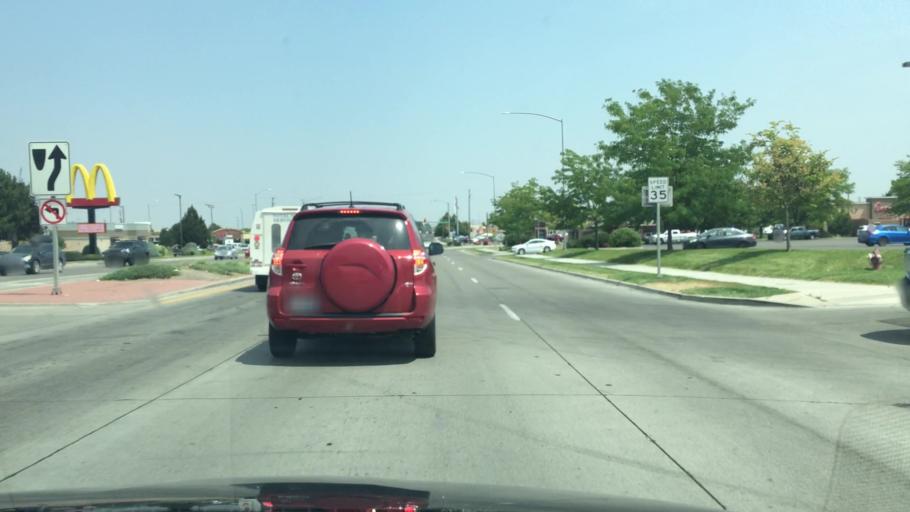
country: US
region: Idaho
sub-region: Twin Falls County
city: Twin Falls
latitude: 42.5919
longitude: -114.4628
